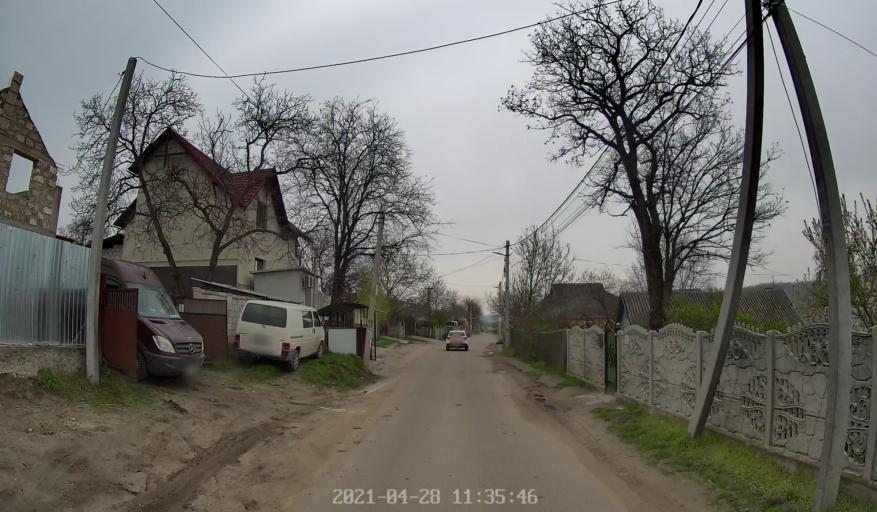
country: MD
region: Chisinau
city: Singera
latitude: 46.9476
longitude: 28.9466
